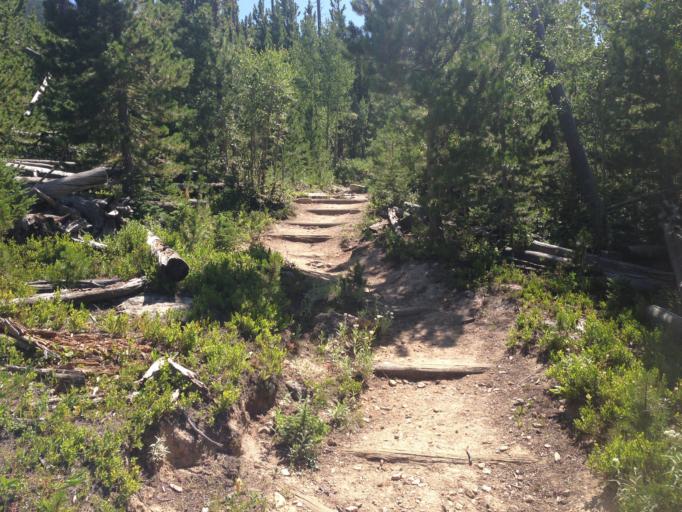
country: US
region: Colorado
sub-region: Larimer County
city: Estes Park
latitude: 40.1965
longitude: -105.5716
